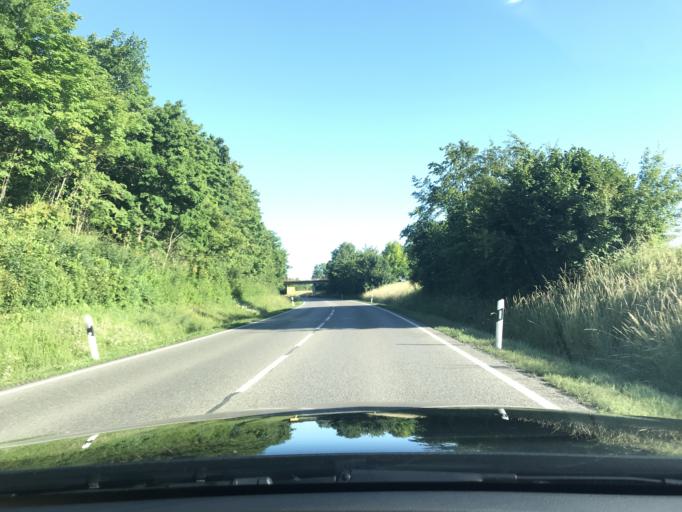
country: DE
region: Baden-Wuerttemberg
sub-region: Regierungsbezirk Stuttgart
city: Stuttgart Muehlhausen
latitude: 48.8311
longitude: 9.2500
